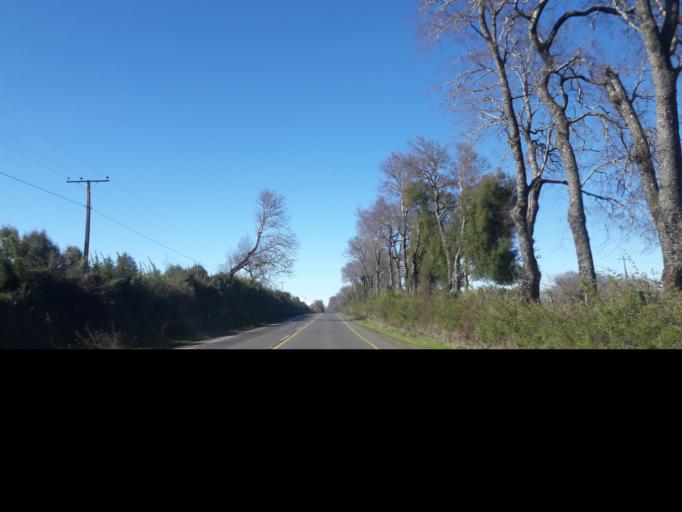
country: CL
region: Araucania
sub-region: Provincia de Malleco
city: Victoria
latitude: -38.2662
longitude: -72.2270
